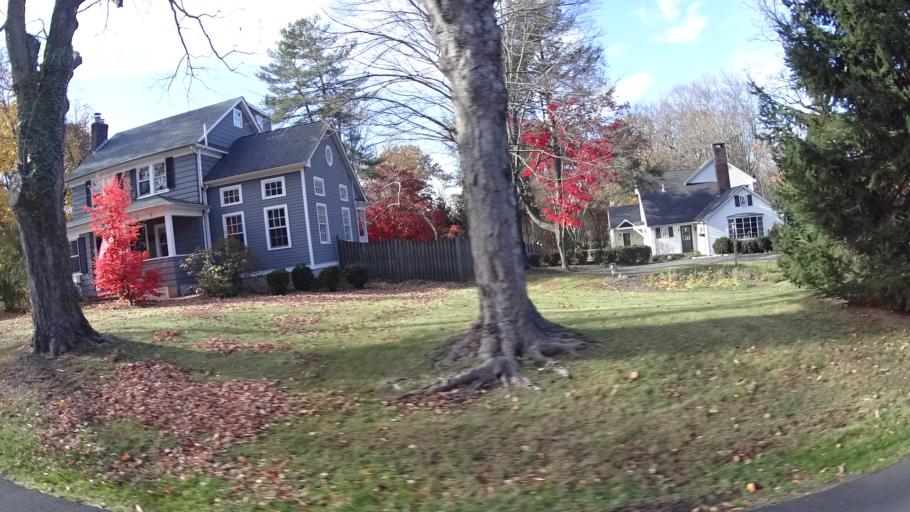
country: US
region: New Jersey
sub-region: Morris County
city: Morristown
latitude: 40.7432
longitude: -74.4993
